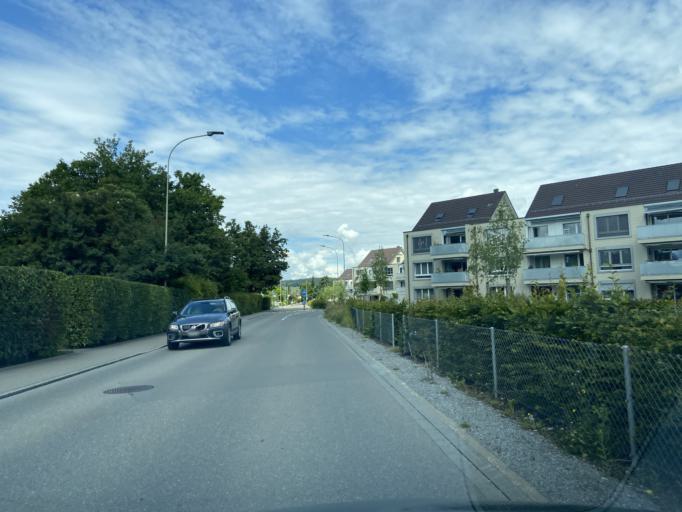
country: CH
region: Zurich
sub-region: Bezirk Winterthur
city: Wiesendangen / Wiesendangen (Dorf)
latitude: 47.5211
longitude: 8.7856
